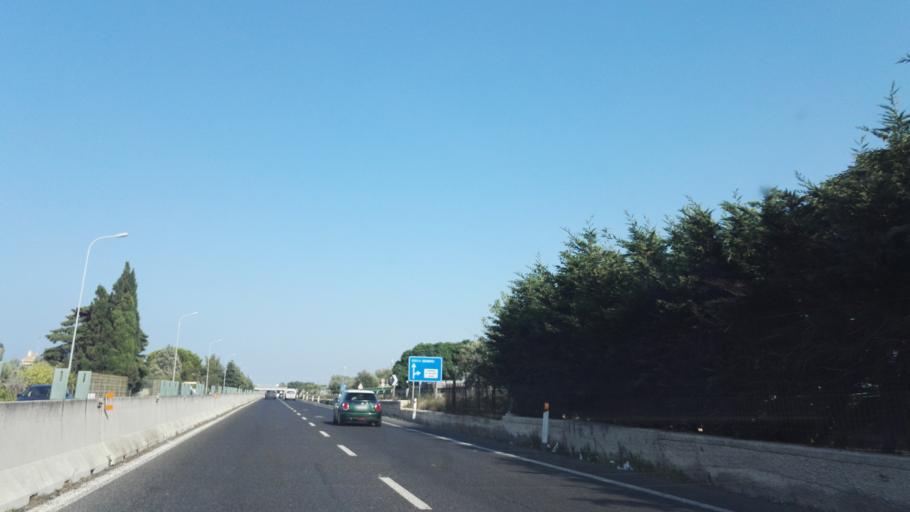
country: IT
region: Apulia
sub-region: Provincia di Bari
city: Parco Scizzo-Parchitello
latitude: 41.0907
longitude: 16.9704
